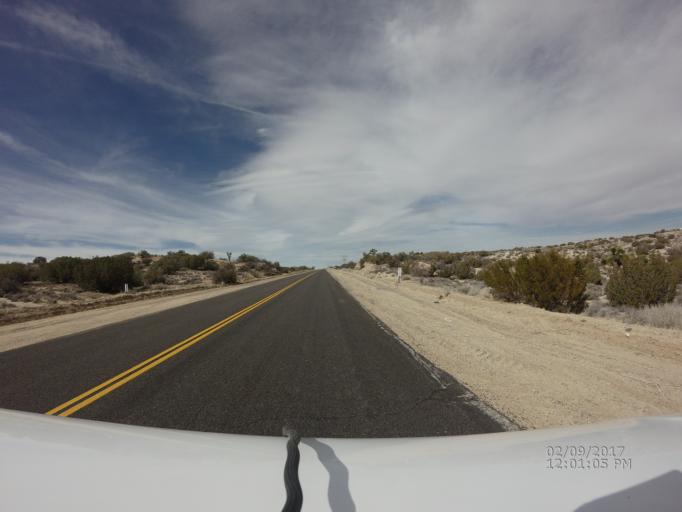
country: US
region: California
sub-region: Los Angeles County
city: Littlerock
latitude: 34.4757
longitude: -117.9023
